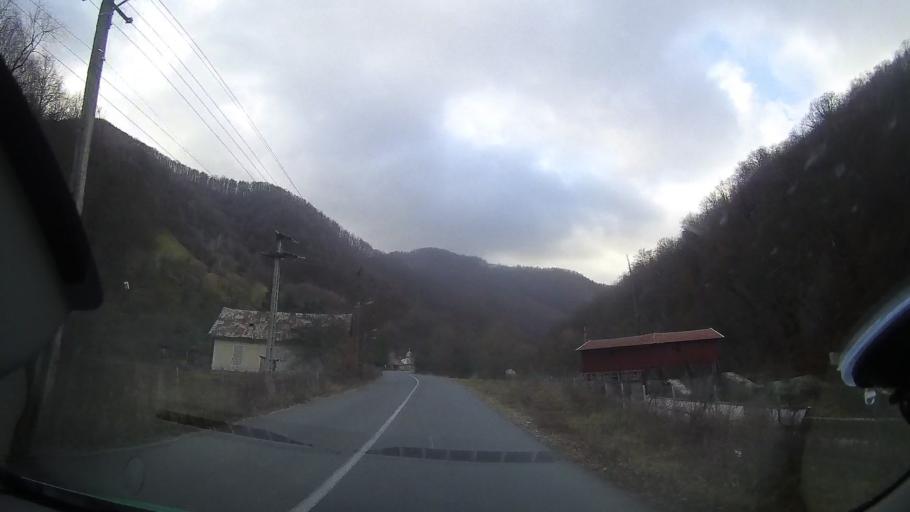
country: RO
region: Cluj
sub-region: Comuna Maguri-Racatau
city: Maguri-Racatau
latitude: 46.6709
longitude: 23.2519
